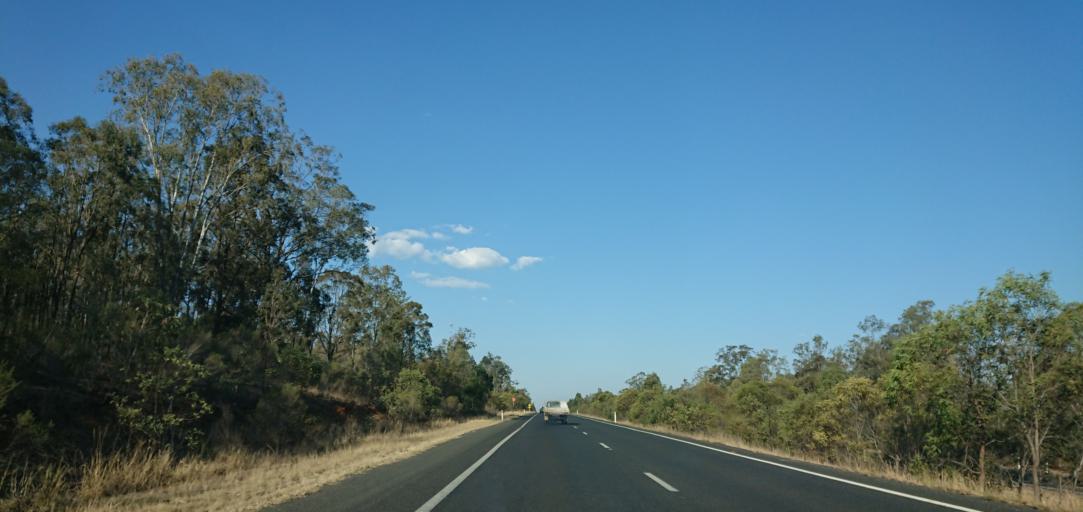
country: AU
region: Queensland
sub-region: Lockyer Valley
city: Gatton
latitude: -27.5532
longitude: 152.1886
